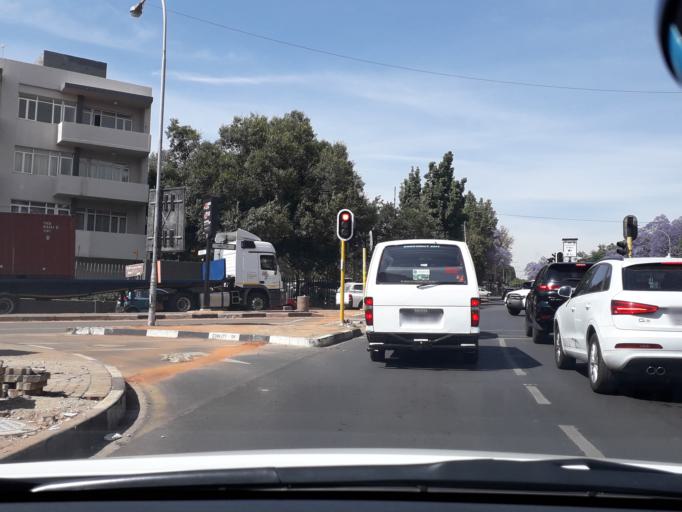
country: ZA
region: Gauteng
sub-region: City of Johannesburg Metropolitan Municipality
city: Johannesburg
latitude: -26.1350
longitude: 28.0482
